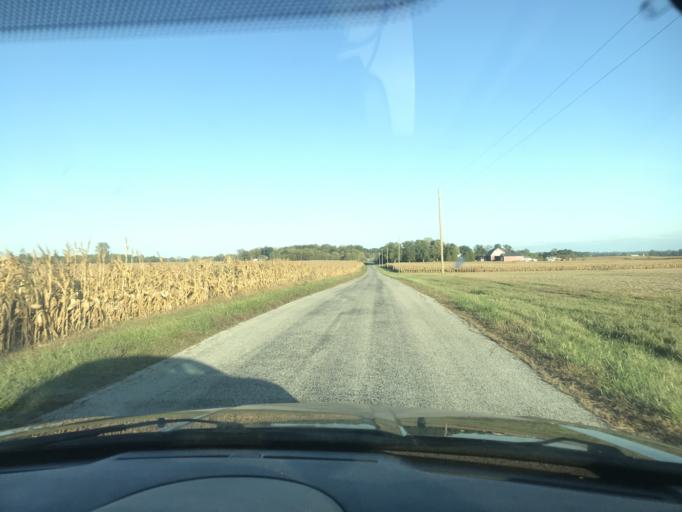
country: US
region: Ohio
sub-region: Logan County
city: West Liberty
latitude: 40.2317
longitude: -83.8066
